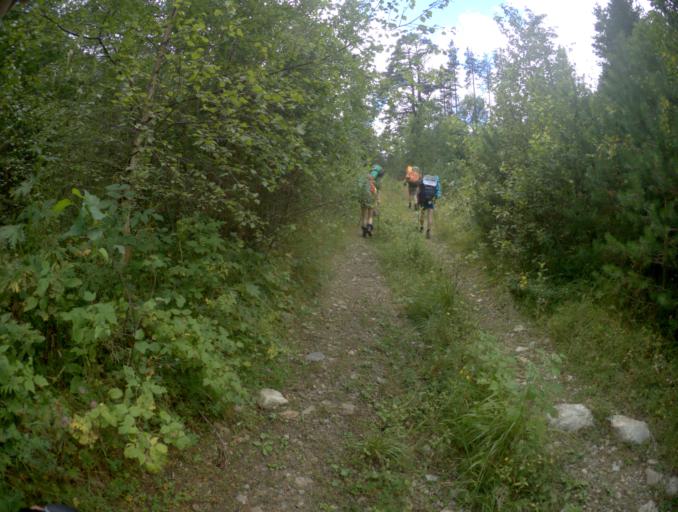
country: RU
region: Karachayevo-Cherkesiya
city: Uchkulan
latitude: 43.3517
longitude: 42.1603
